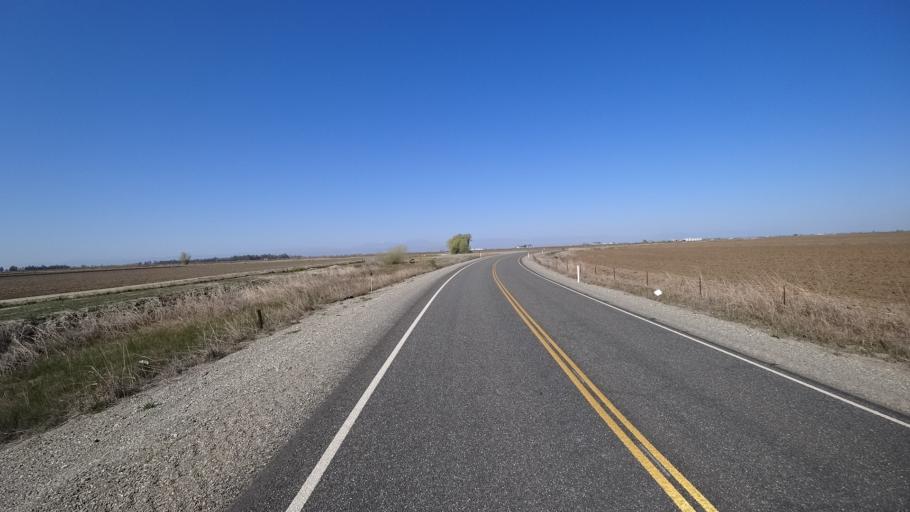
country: US
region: California
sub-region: Glenn County
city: Willows
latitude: 39.4581
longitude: -122.0939
